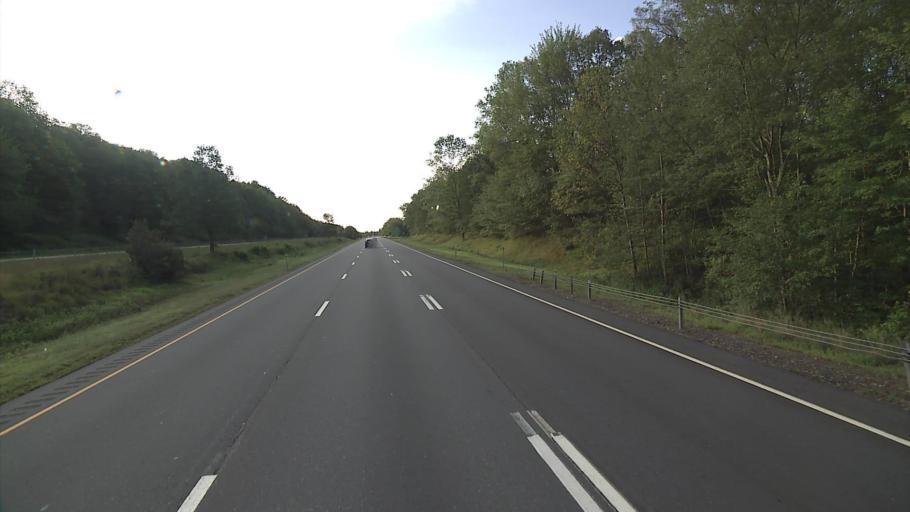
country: US
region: Connecticut
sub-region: New London County
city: Colchester
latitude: 41.5794
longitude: -72.3550
